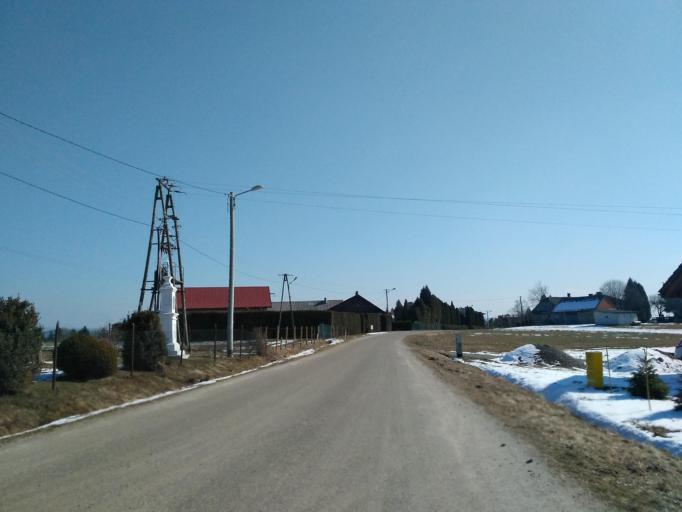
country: PL
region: Subcarpathian Voivodeship
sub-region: Powiat brzozowski
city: Jasienica Rosielna
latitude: 49.7710
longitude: 21.9162
